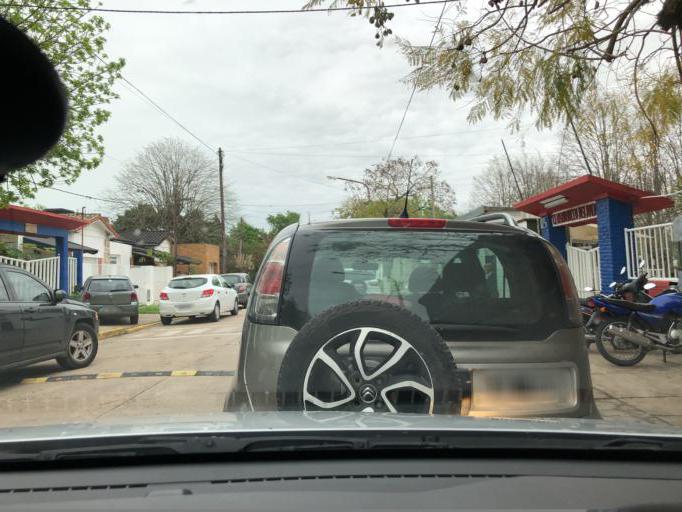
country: AR
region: Buenos Aires
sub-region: Partido de Ensenada
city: Ensenada
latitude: -34.8491
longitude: -57.9205
